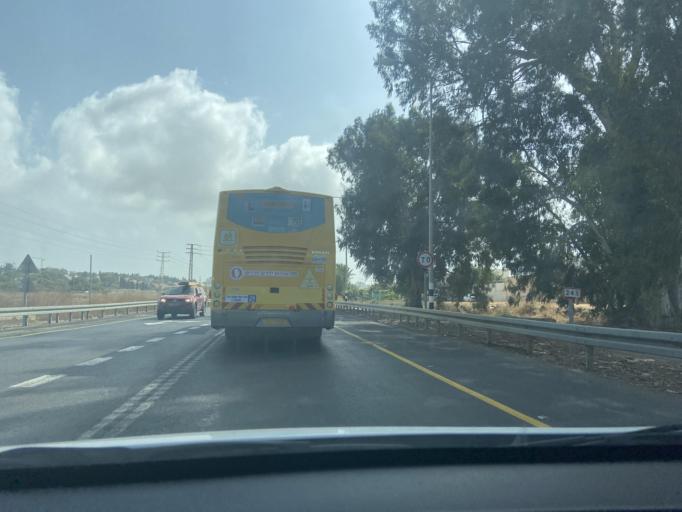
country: IL
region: Northern District
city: Nahariya
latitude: 33.0322
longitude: 35.1043
